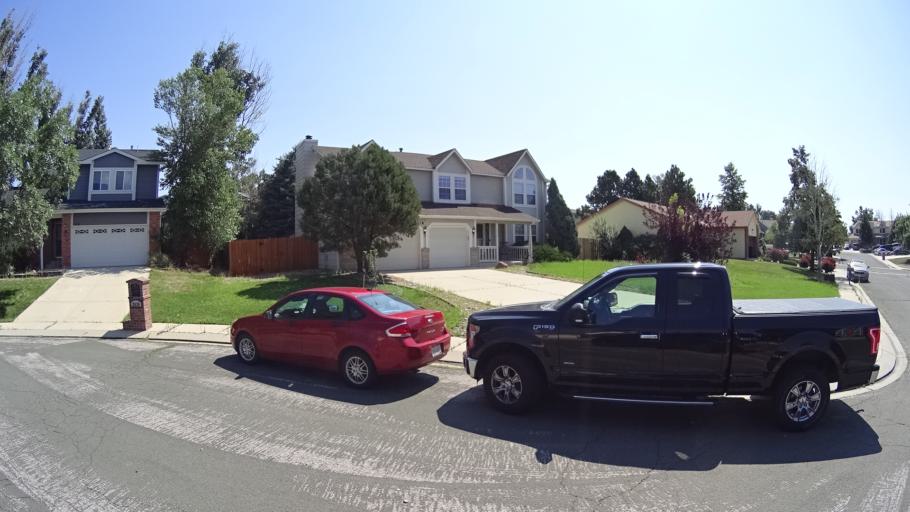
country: US
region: Colorado
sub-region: El Paso County
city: Air Force Academy
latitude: 38.9569
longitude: -104.7788
